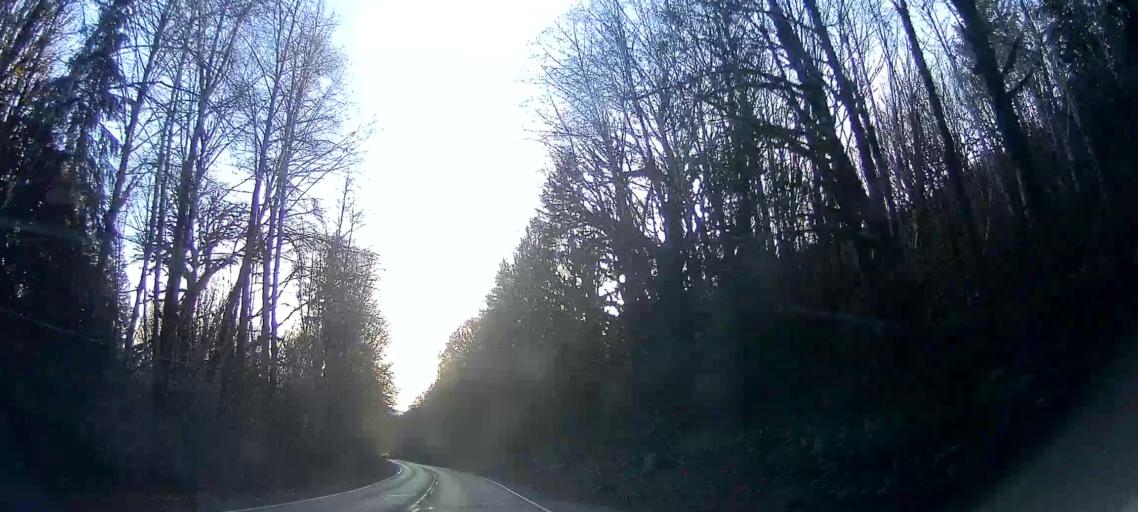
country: US
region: Washington
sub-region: Snohomish County
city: Darrington
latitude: 48.5788
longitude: -121.7771
